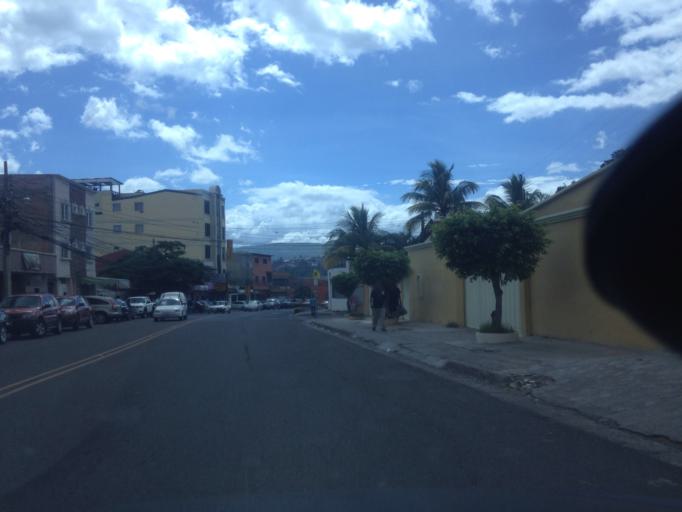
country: HN
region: Francisco Morazan
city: Tegucigalpa
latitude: 14.0771
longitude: -87.1901
